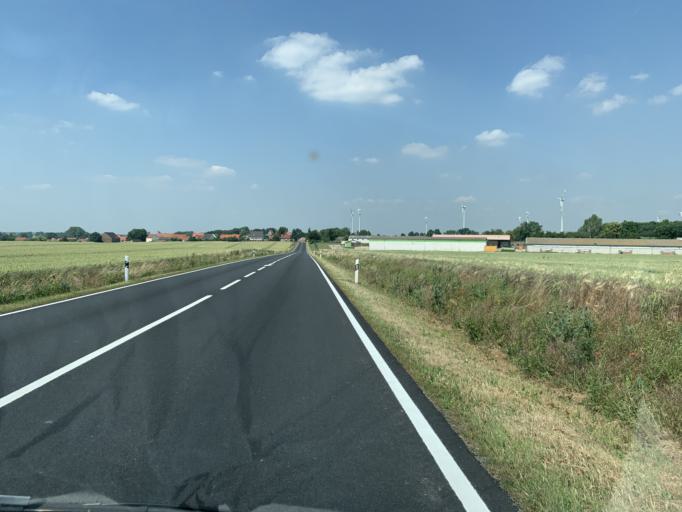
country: DE
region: Saxony-Anhalt
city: Erxleben
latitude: 52.1749
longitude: 11.2682
